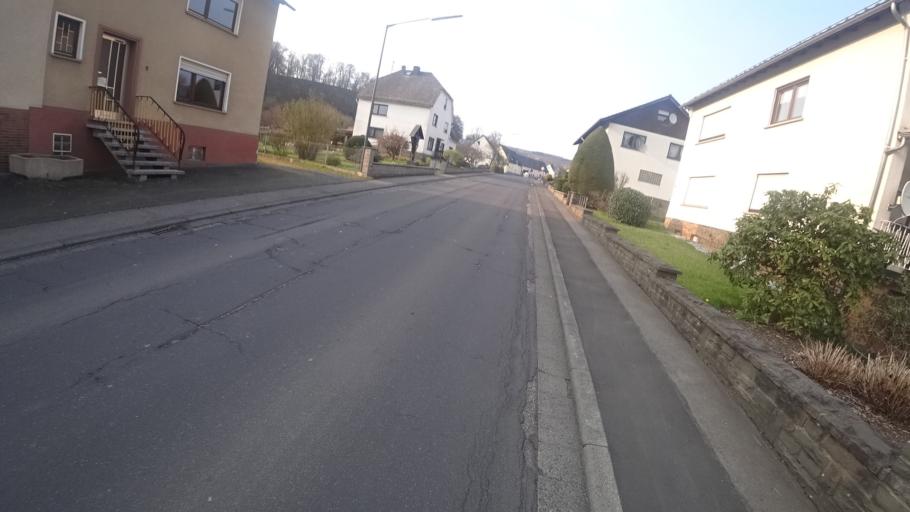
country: DE
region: Rheinland-Pfalz
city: Luckenbach
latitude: 50.7017
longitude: 7.8333
